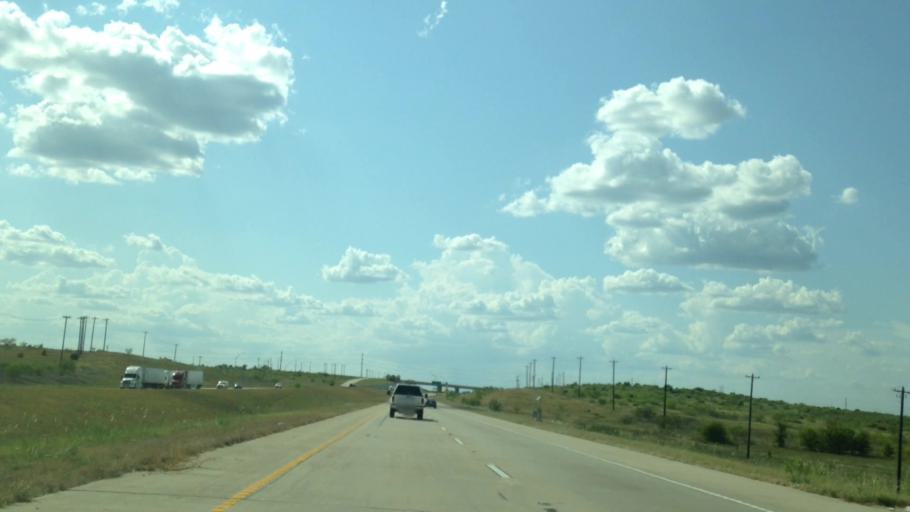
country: US
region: Texas
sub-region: Travis County
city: Onion Creek
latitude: 30.0982
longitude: -97.7721
